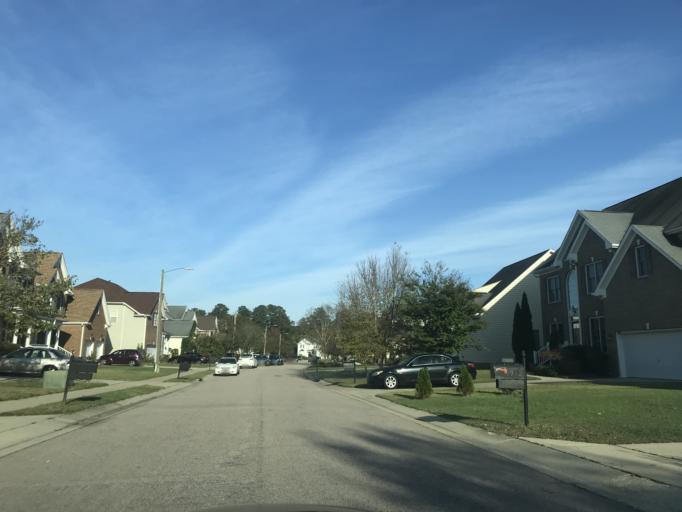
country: US
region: North Carolina
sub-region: Wake County
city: Rolesville
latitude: 35.8894
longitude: -78.5411
